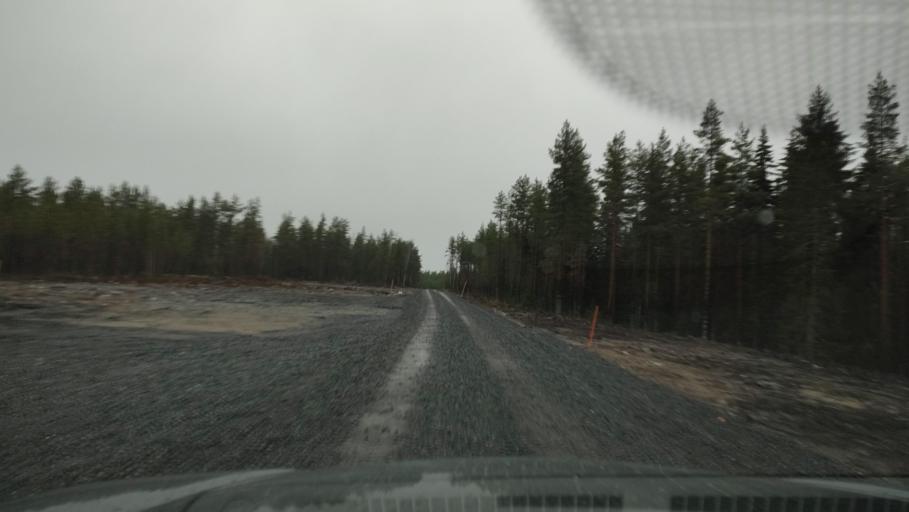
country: FI
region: Southern Ostrobothnia
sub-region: Suupohja
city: Karijoki
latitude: 62.1449
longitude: 21.6266
